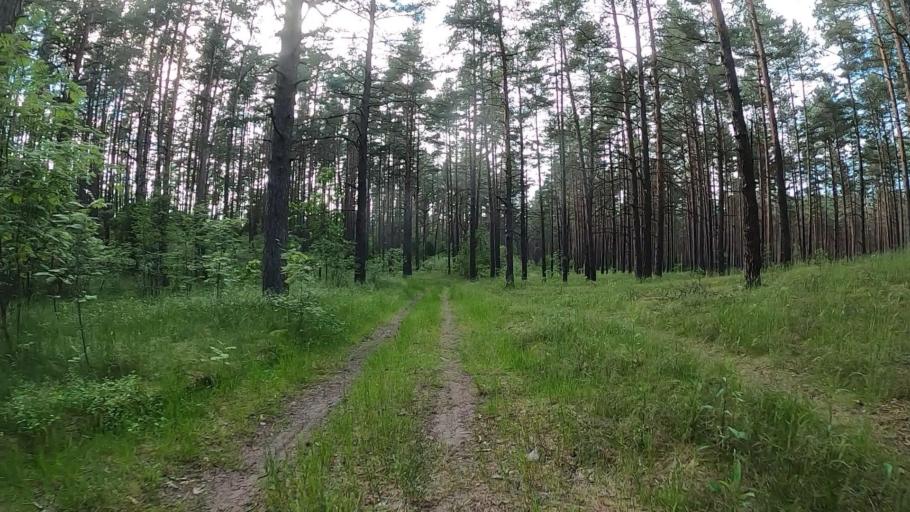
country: LV
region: Riga
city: Bergi
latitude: 57.0070
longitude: 24.2489
